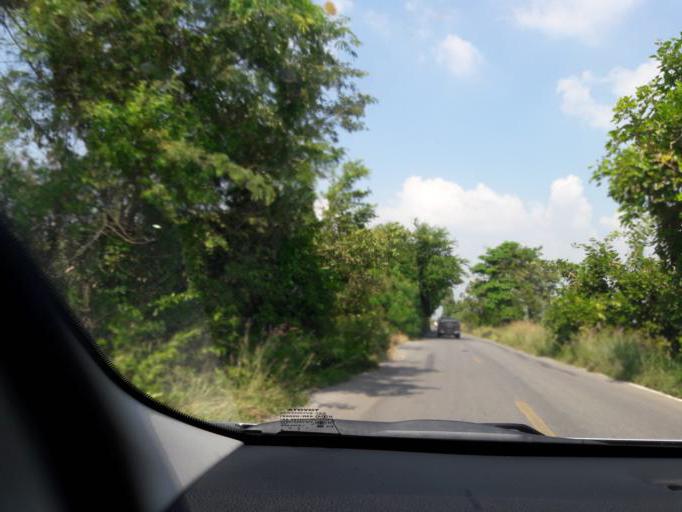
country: TH
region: Ang Thong
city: Ang Thong
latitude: 14.5903
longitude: 100.4004
